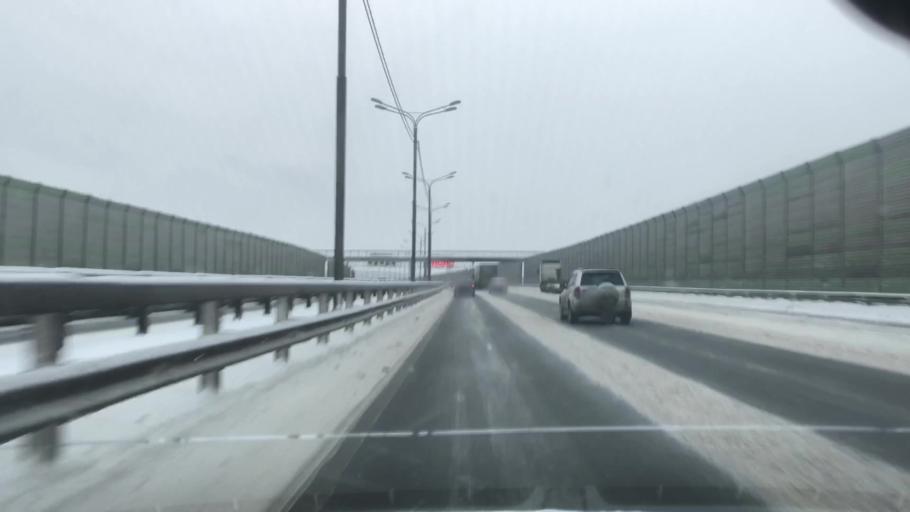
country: RU
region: Moskovskaya
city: Belyye Stolby
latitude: 55.3179
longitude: 37.8148
